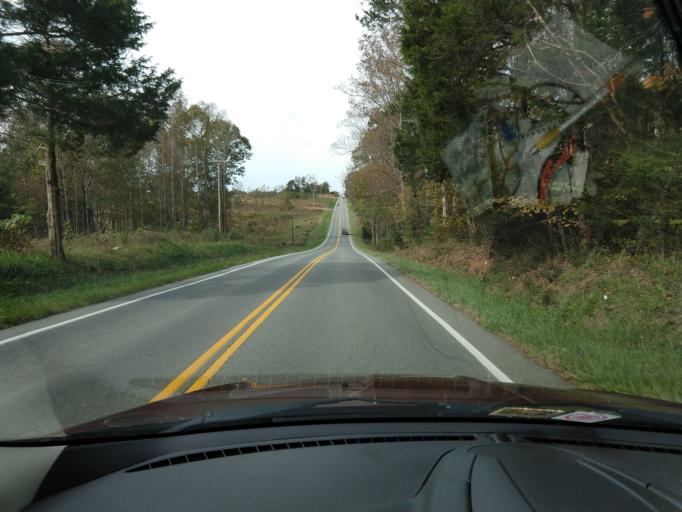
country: US
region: Virginia
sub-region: Franklin County
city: Union Hall
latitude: 36.9890
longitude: -79.6605
